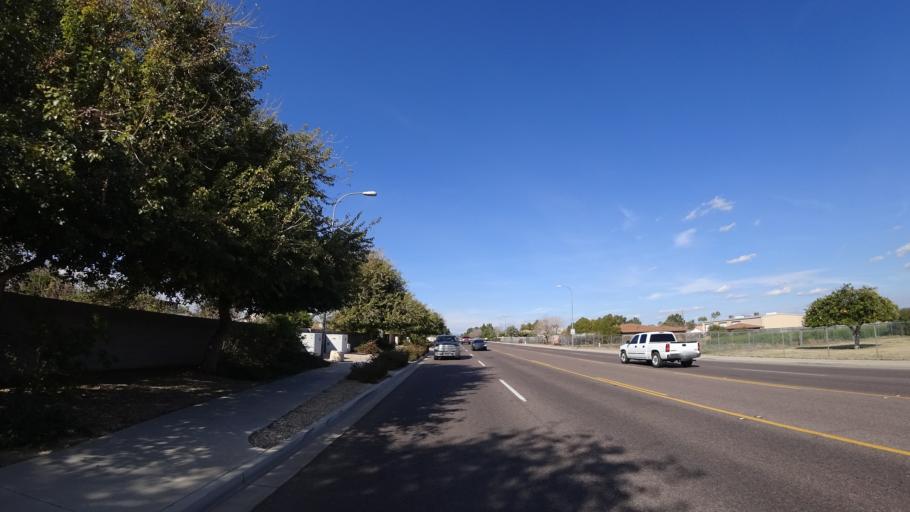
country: US
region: Arizona
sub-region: Maricopa County
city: Peoria
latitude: 33.6180
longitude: -112.2201
